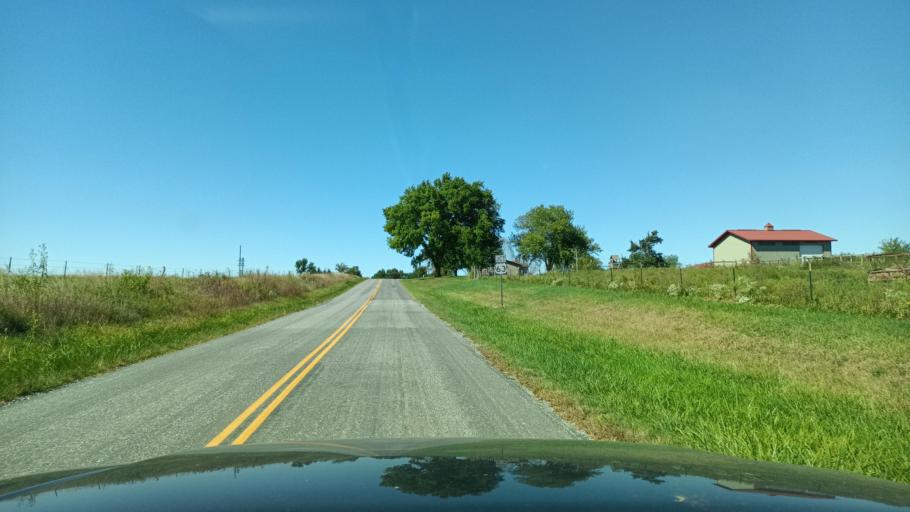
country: US
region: Missouri
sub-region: Adair County
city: Kirksville
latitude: 40.3298
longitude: -92.5609
